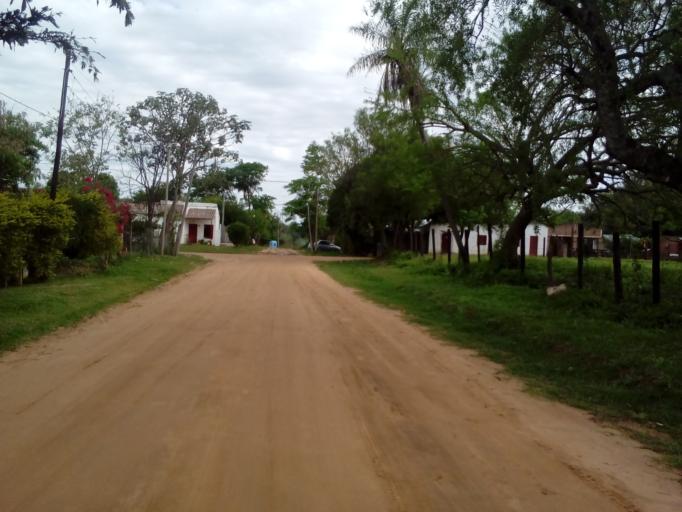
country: AR
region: Corrientes
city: San Luis del Palmar
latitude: -27.4573
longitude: -58.6558
